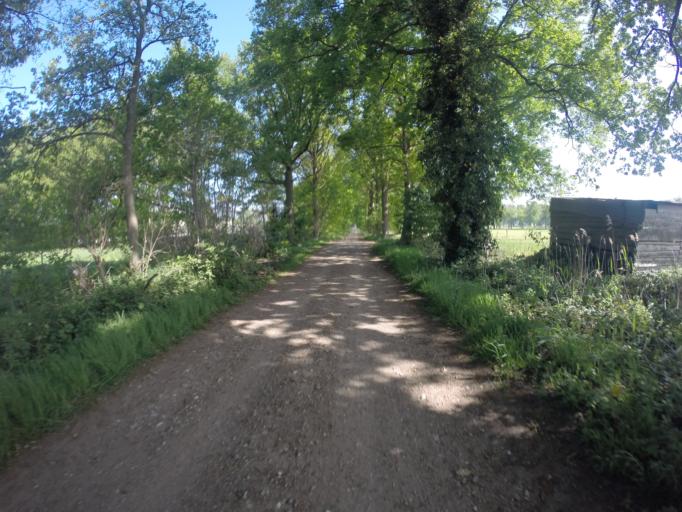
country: BE
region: Flanders
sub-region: Provincie Oost-Vlaanderen
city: Knesselare
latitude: 51.1592
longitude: 3.4320
